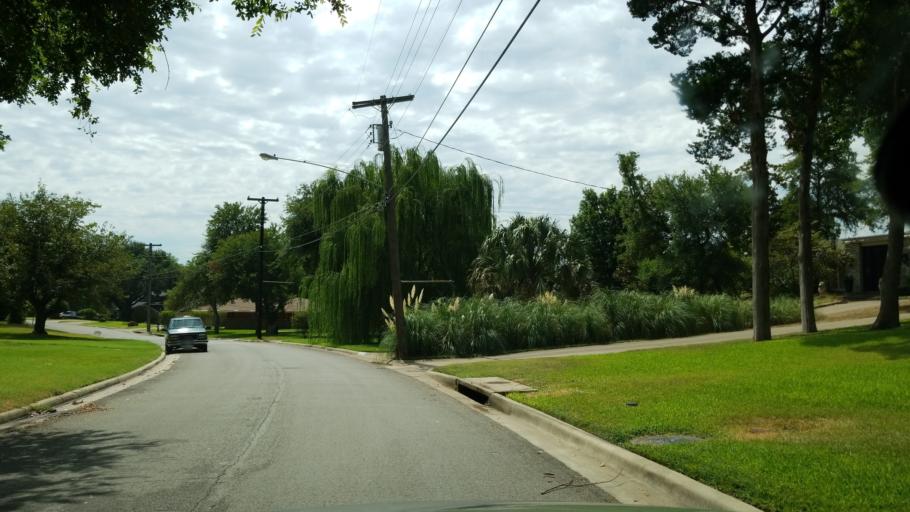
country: US
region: Texas
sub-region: Dallas County
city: Duncanville
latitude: 32.6703
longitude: -96.8491
